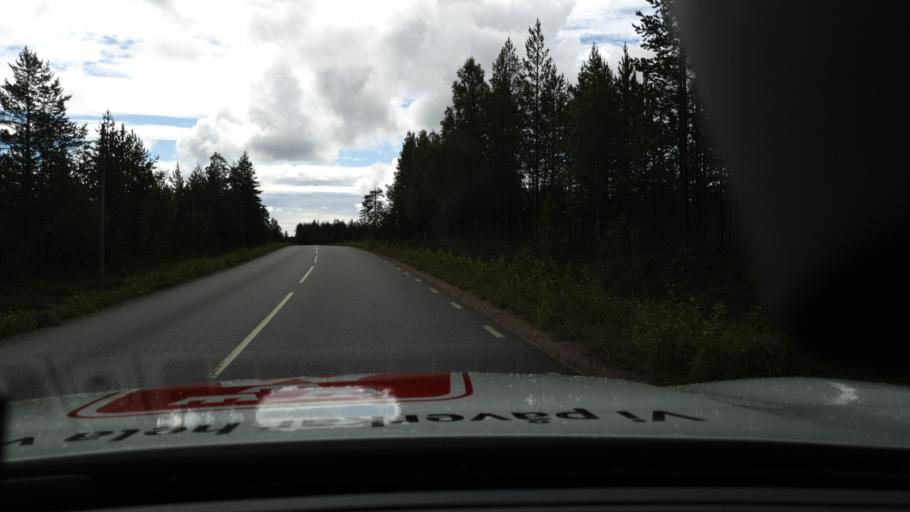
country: SE
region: Norrbotten
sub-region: Lulea Kommun
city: Sodra Sunderbyn
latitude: 65.4996
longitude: 21.8738
